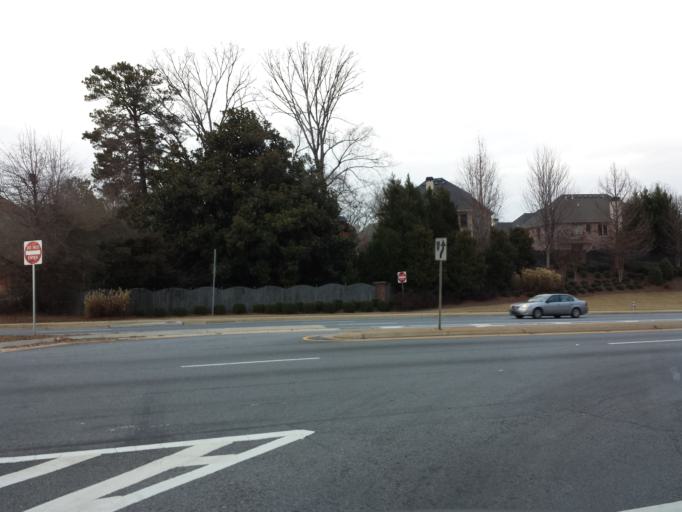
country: US
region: Georgia
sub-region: Cobb County
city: Marietta
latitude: 33.9742
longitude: -84.4776
